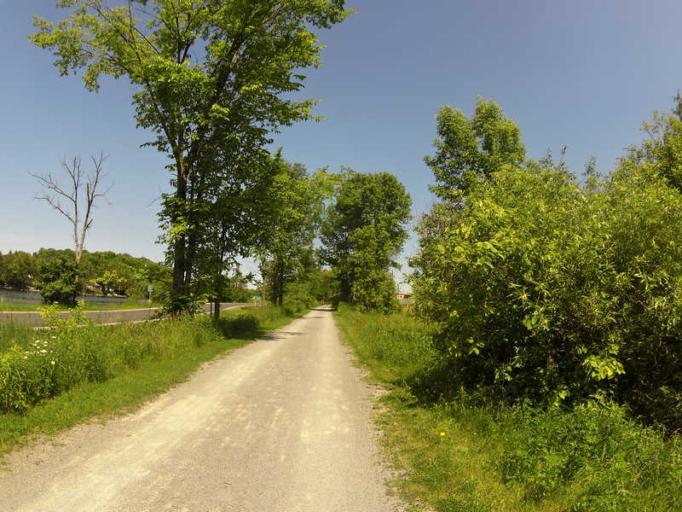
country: CA
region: Ontario
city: Peterborough
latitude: 44.4158
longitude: -78.2642
